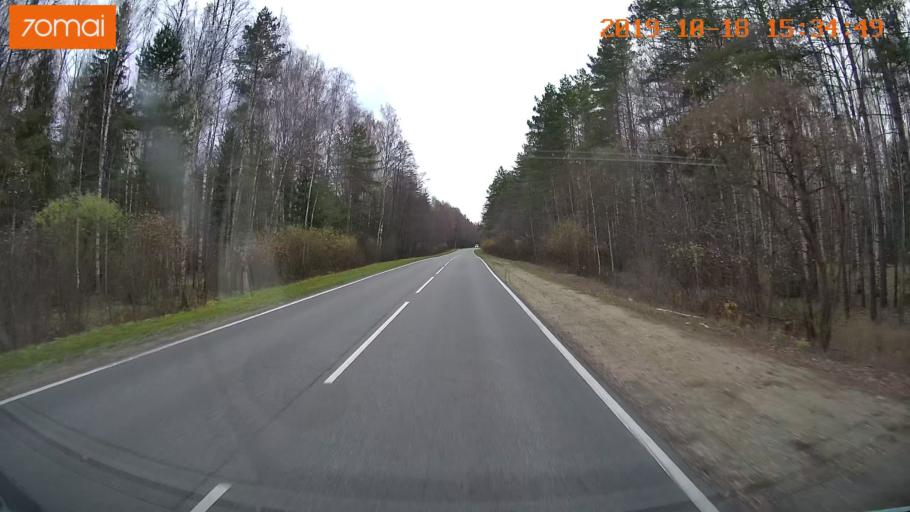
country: RU
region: Vladimir
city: Anopino
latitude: 55.8591
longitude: 40.6377
